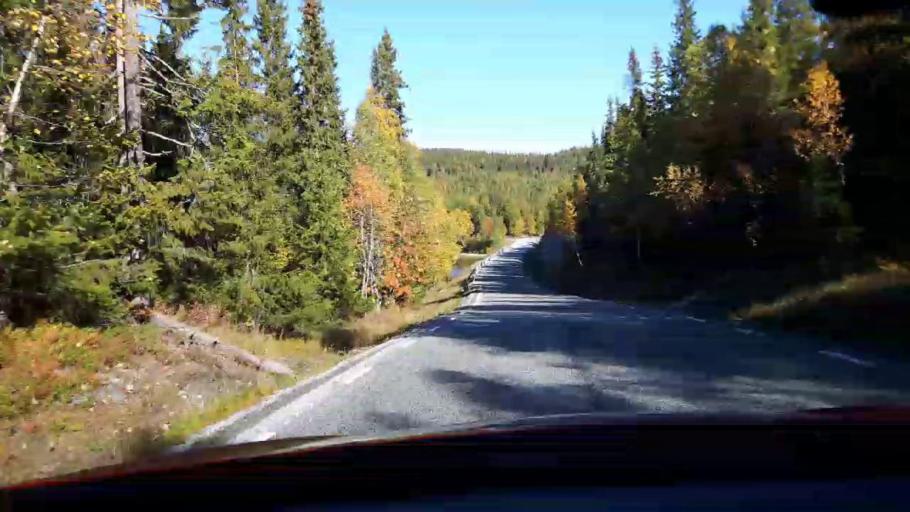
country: NO
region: Nord-Trondelag
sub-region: Royrvik
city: Royrvik
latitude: 64.8160
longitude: 14.1825
